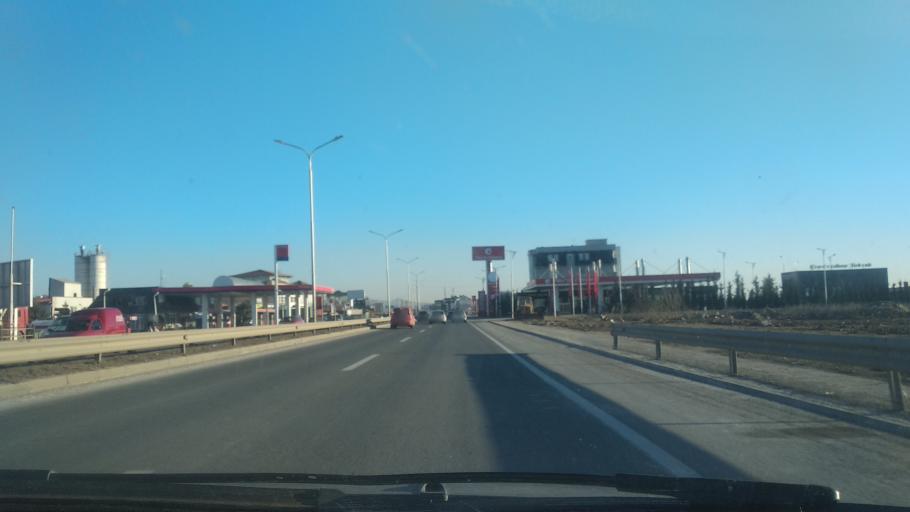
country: XK
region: Pristina
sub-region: Kosovo Polje
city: Kosovo Polje
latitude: 42.6626
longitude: 21.1298
